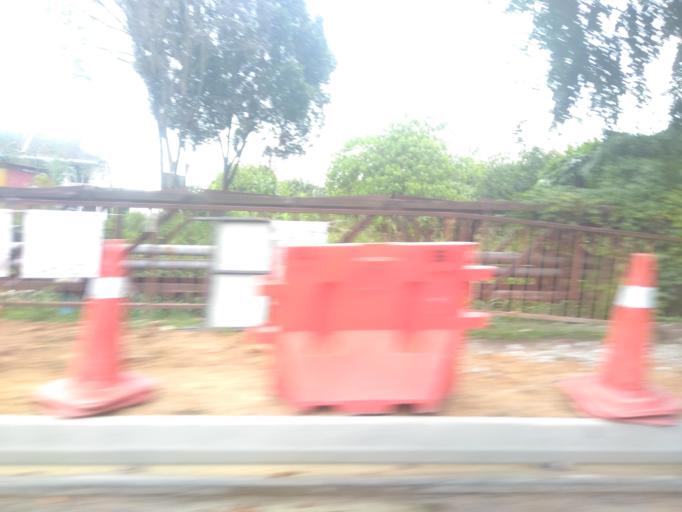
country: MY
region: Penang
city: Bukit Mertajam
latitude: 5.3327
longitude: 100.4829
